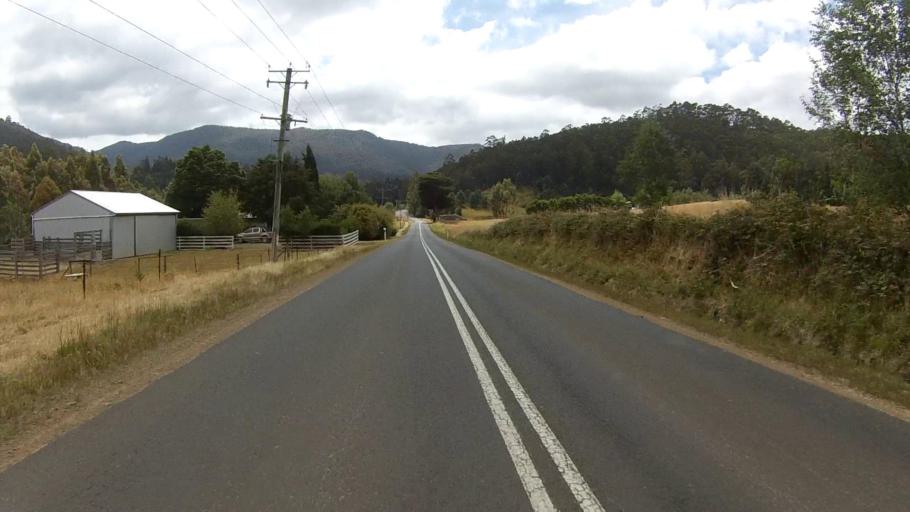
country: AU
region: Tasmania
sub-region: Huon Valley
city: Cygnet
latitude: -43.1358
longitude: 147.1542
